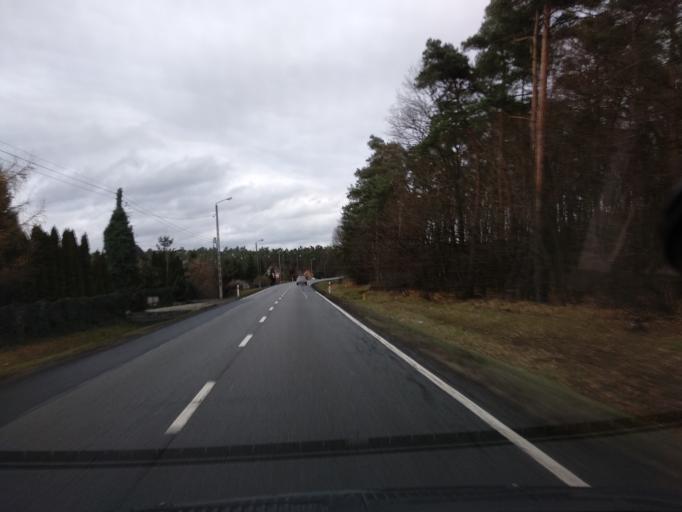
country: PL
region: Lower Silesian Voivodeship
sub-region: Powiat olesnicki
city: Olesnica
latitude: 51.2339
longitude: 17.4511
